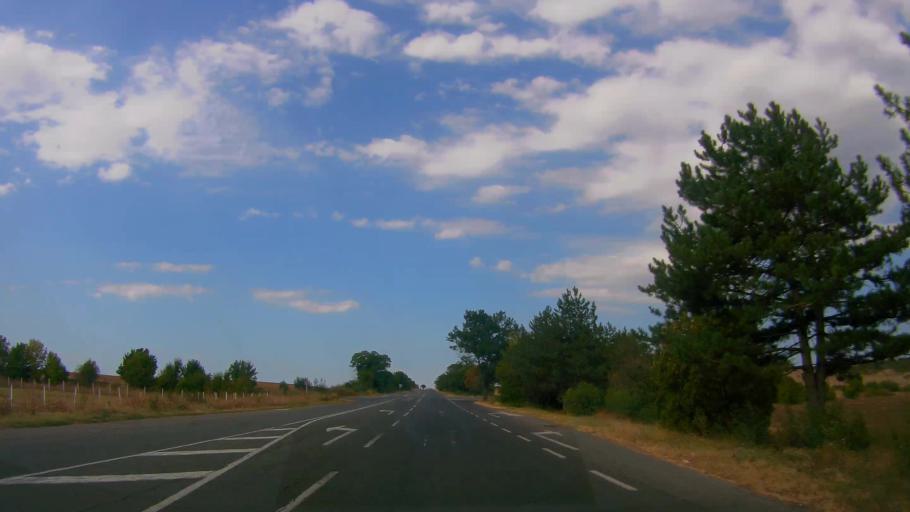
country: BG
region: Burgas
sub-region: Obshtina Aytos
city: Aytos
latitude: 42.6965
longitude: 27.1922
